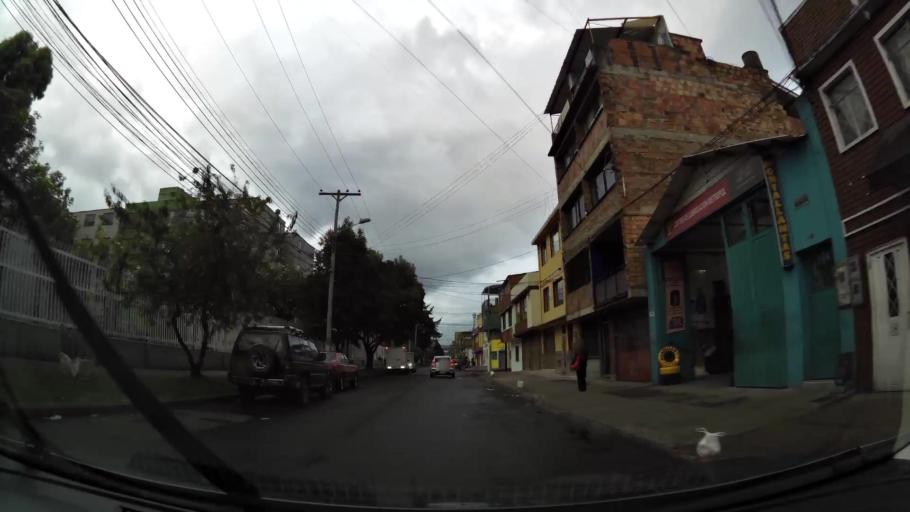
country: CO
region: Bogota D.C.
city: Barrio San Luis
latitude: 4.6789
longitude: -74.0805
